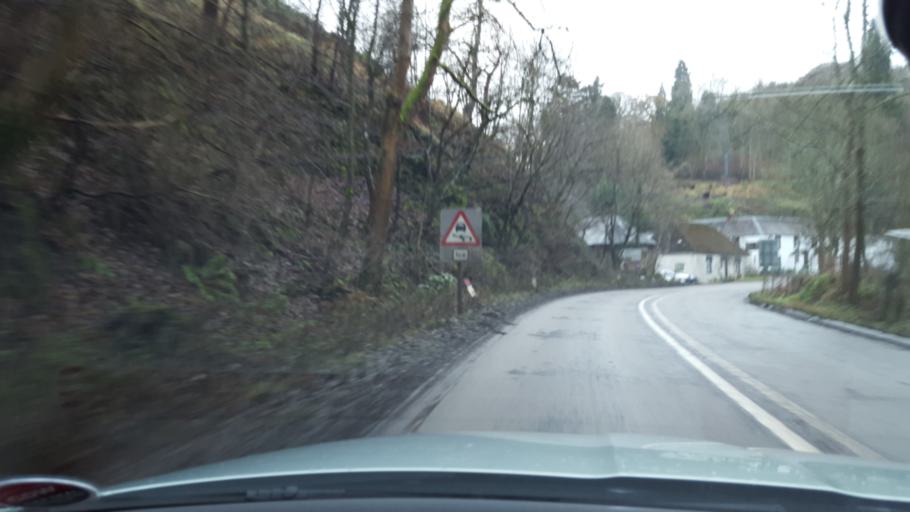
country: GB
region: Scotland
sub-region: Perth and Kinross
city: Abernethy
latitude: 56.3034
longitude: -3.3577
